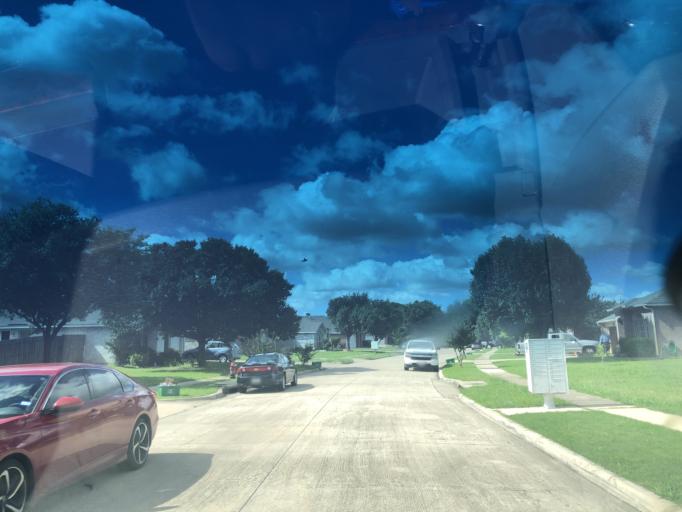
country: US
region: Texas
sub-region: Dallas County
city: Grand Prairie
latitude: 32.6947
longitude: -97.0315
